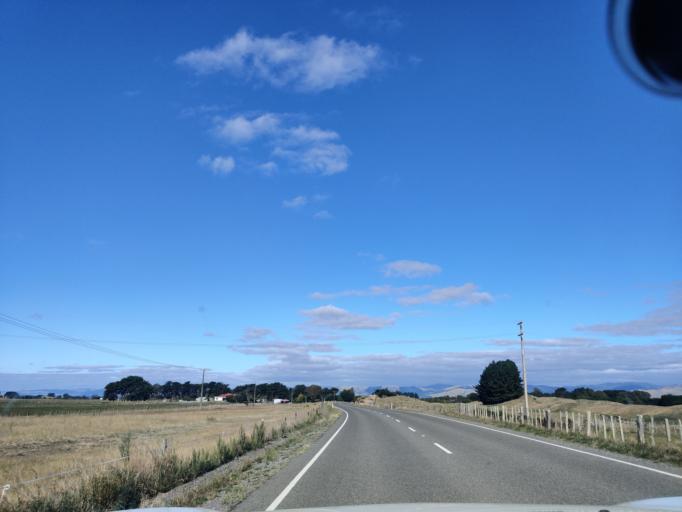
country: NZ
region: Manawatu-Wanganui
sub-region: Horowhenua District
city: Foxton
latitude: -40.4149
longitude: 175.4007
